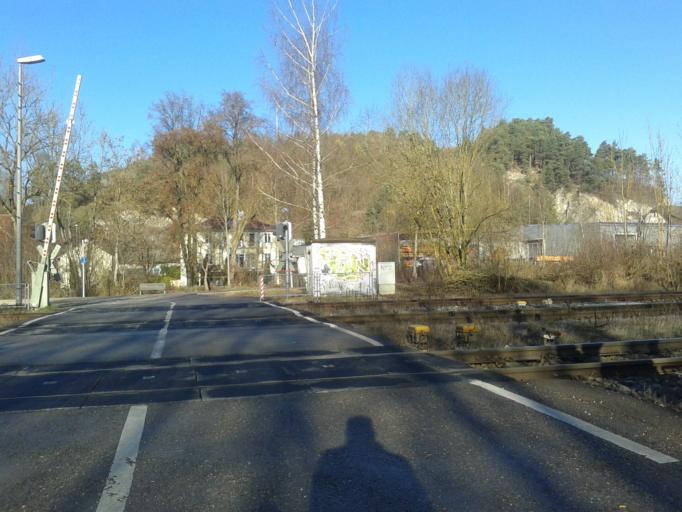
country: DE
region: Baden-Wuerttemberg
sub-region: Tuebingen Region
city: Dornstadt
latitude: 48.4183
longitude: 9.9009
